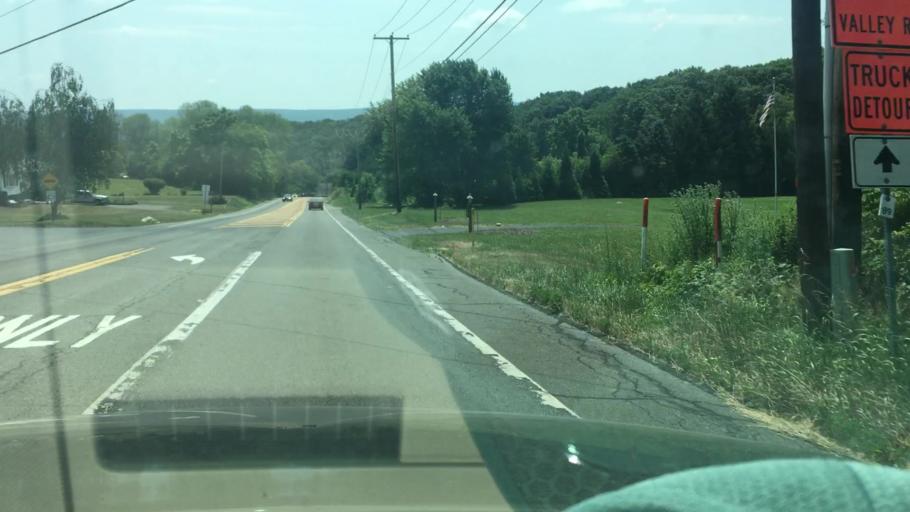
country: US
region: Pennsylvania
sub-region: Schuylkill County
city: Coaldale
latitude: 40.7503
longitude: -75.9039
